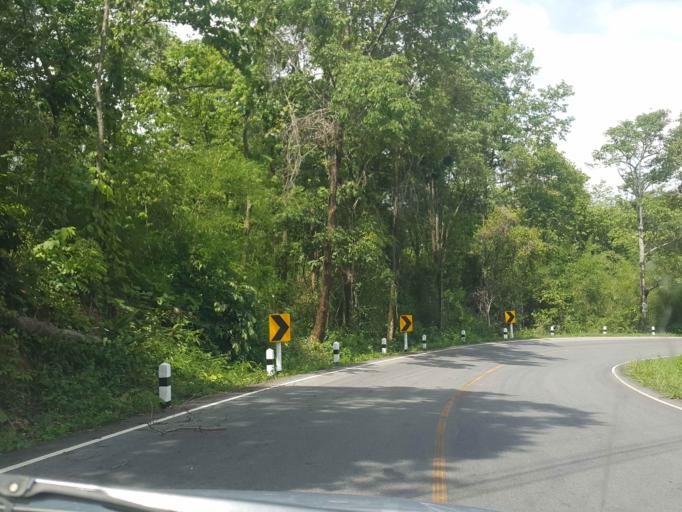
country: TH
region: Nan
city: Ban Luang
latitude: 18.8778
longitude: 100.5412
